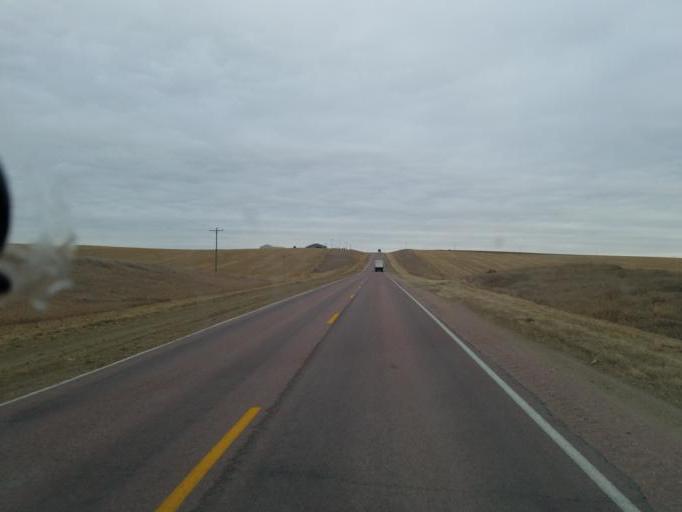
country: US
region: Nebraska
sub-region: Cedar County
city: Hartington
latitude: 42.4675
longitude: -97.1997
